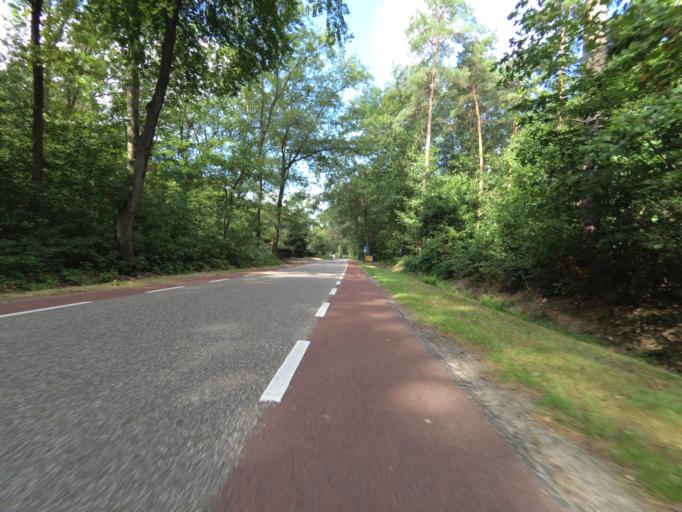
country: NL
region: Overijssel
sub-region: Gemeente Oldenzaal
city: Oldenzaal
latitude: 52.3087
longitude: 6.8906
